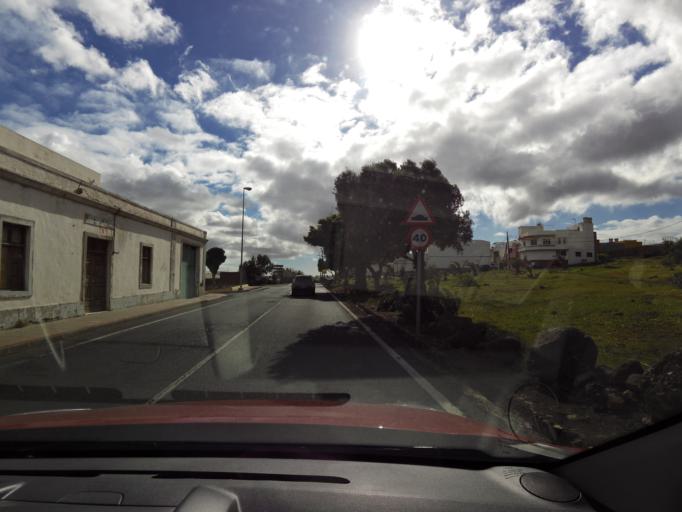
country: ES
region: Canary Islands
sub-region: Provincia de Las Palmas
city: Ingenio
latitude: 27.9136
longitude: -15.4396
